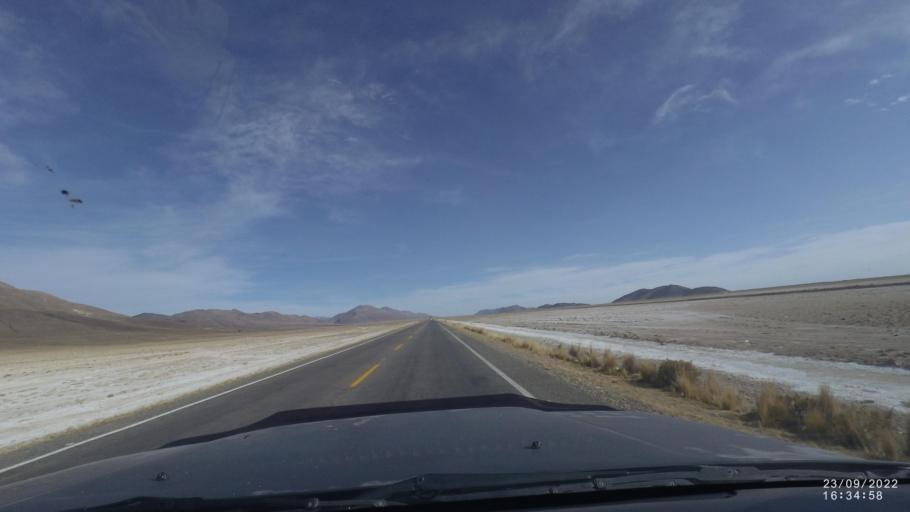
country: BO
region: Oruro
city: Machacamarca
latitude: -18.1972
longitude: -67.0126
